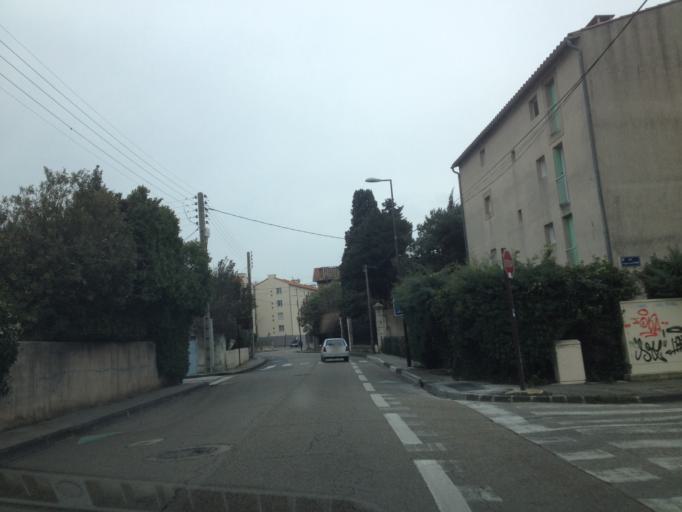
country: FR
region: Provence-Alpes-Cote d'Azur
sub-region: Departement du Vaucluse
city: Avignon
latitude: 43.9375
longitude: 4.8163
